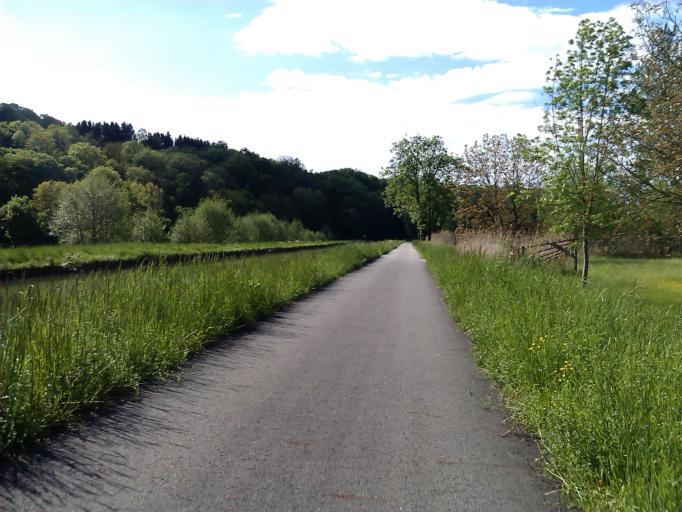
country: FR
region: Franche-Comte
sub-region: Departement du Doubs
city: Montenois
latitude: 47.4313
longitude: 6.6056
